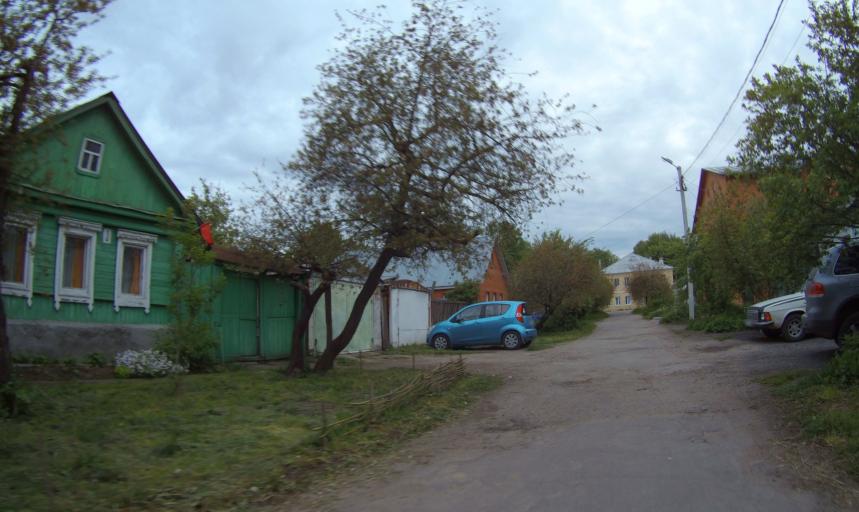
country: RU
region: Moskovskaya
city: Kolomna
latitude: 55.0980
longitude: 38.7731
